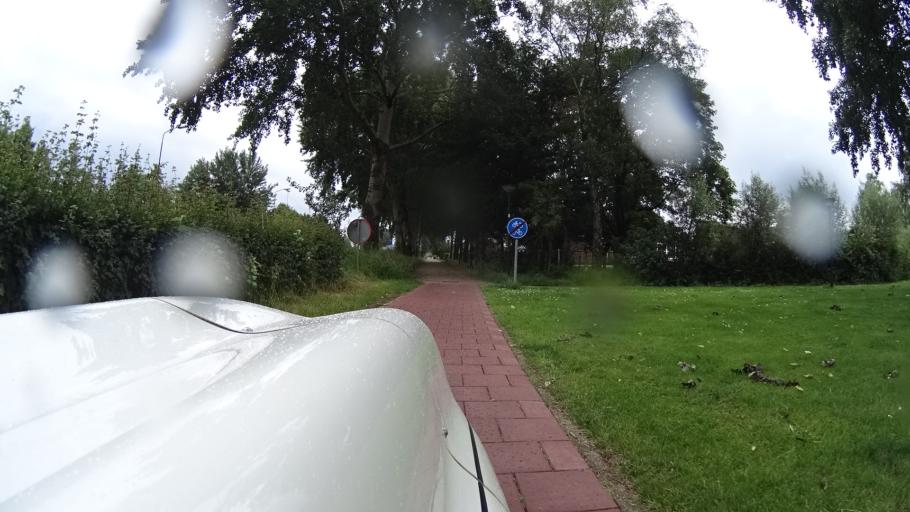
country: NL
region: North Brabant
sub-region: Gemeente Veghel
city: Eerde
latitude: 51.6060
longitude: 5.4987
